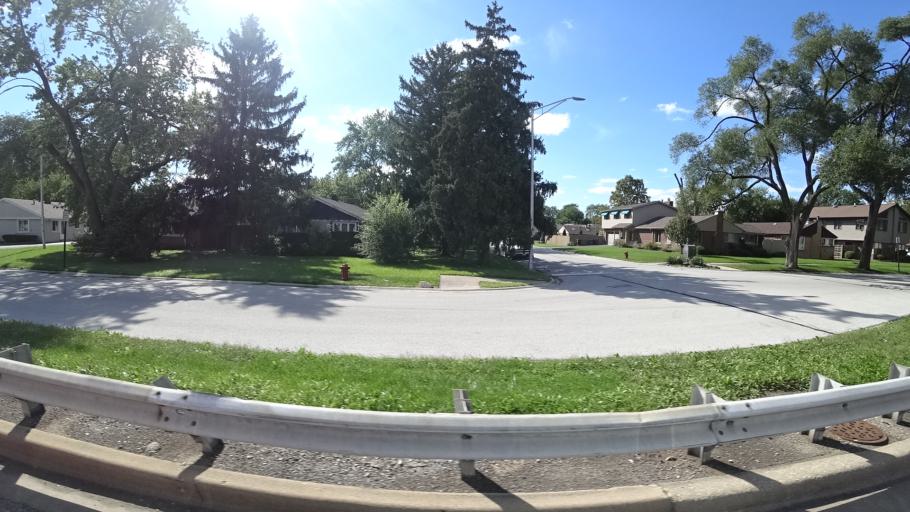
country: US
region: Illinois
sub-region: Cook County
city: Oak Lawn
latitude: 41.7119
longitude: -87.7406
